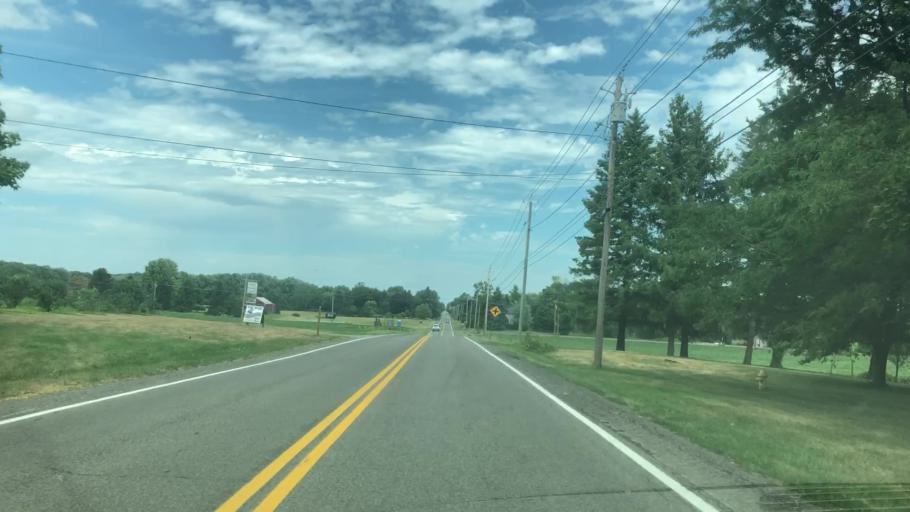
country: US
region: New York
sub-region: Monroe County
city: Webster
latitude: 43.1716
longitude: -77.4005
